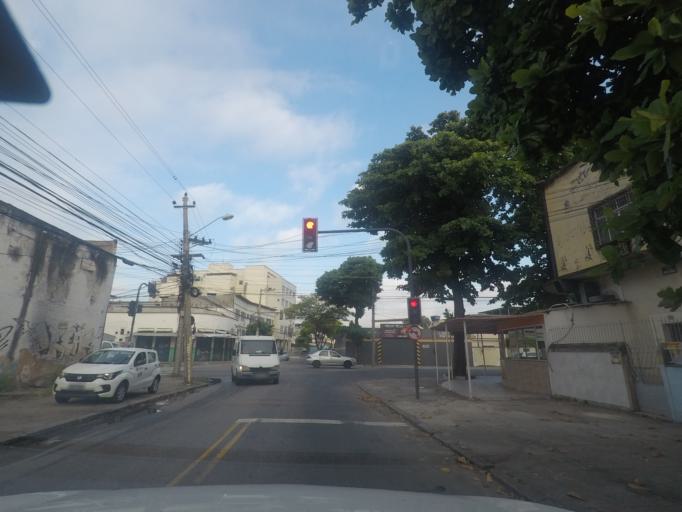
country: BR
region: Rio de Janeiro
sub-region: Duque De Caxias
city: Duque de Caxias
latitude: -22.8330
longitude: -43.2763
